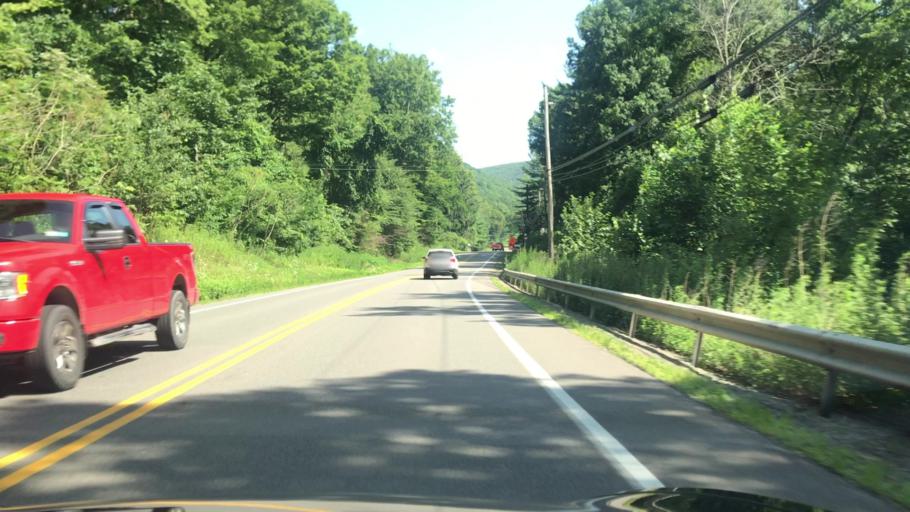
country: US
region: Pennsylvania
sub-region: Lycoming County
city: Kenmar
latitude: 41.4715
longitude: -76.9810
